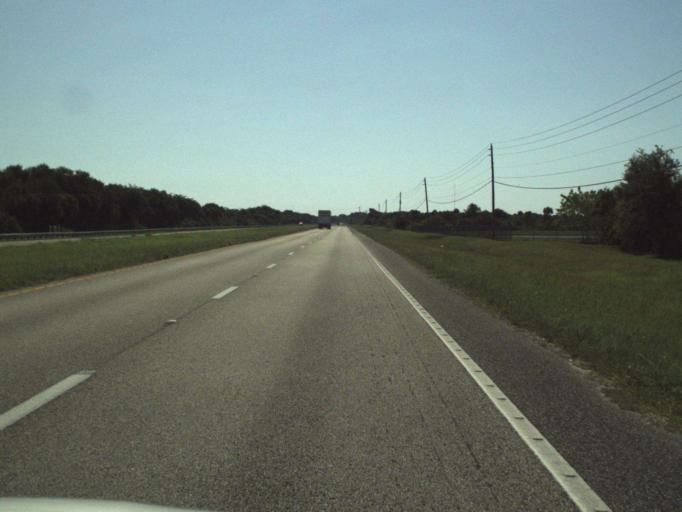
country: US
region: Florida
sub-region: Brevard County
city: Cocoa West
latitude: 28.3644
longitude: -80.8441
